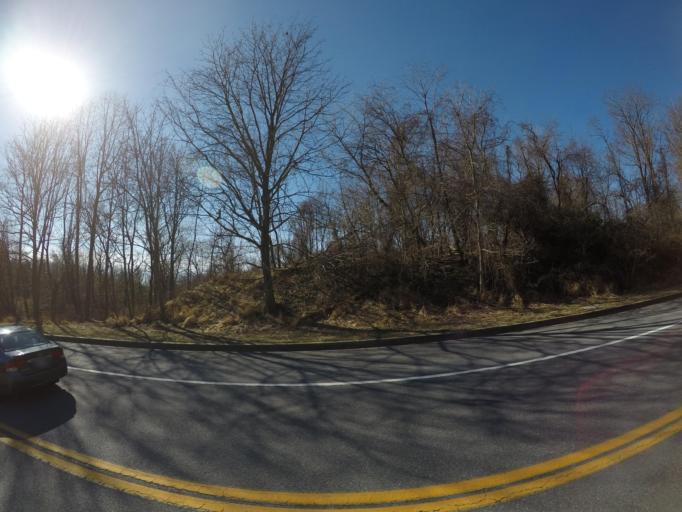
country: US
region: Maryland
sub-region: Howard County
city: Columbia
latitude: 39.2385
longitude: -76.8311
